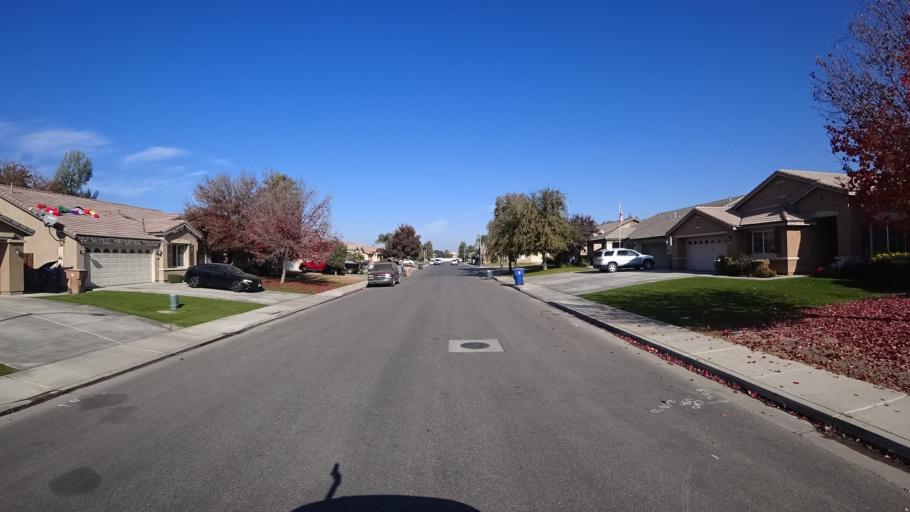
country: US
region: California
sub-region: Kern County
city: Greenfield
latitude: 35.2681
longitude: -119.0606
